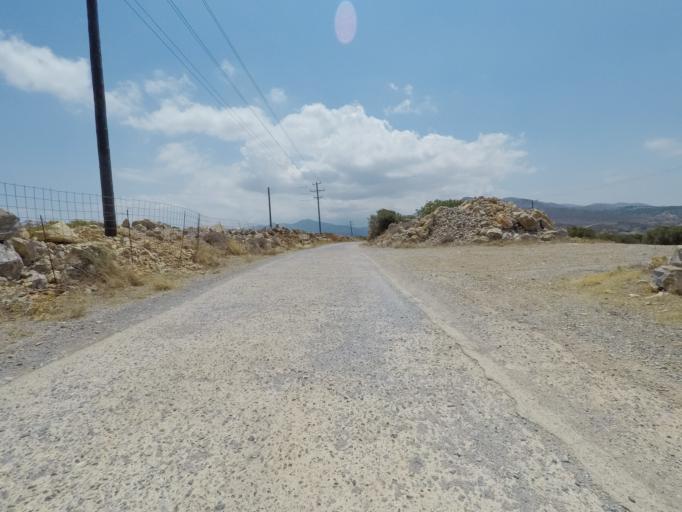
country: GR
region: Crete
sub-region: Nomos Lasithiou
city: Elounda
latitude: 35.3147
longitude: 25.7432
